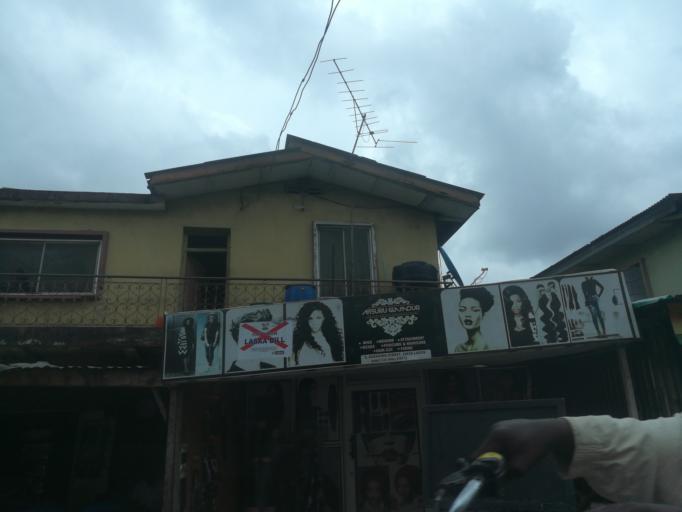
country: NG
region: Lagos
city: Ikeja
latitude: 6.5982
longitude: 3.3444
